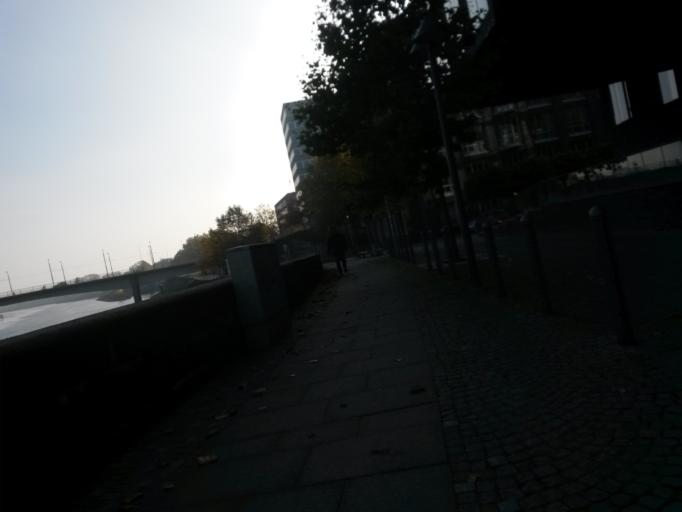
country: DE
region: Bremen
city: Bremen
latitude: 53.0738
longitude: 8.8025
